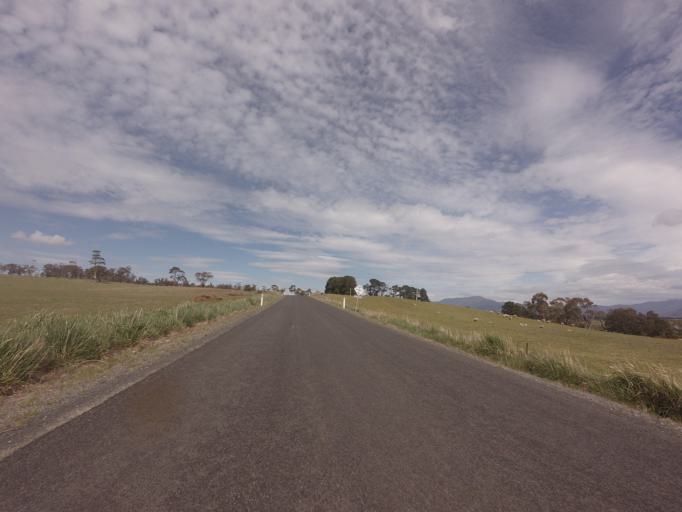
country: AU
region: Tasmania
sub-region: Northern Midlands
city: Longford
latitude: -41.7605
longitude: 147.2087
